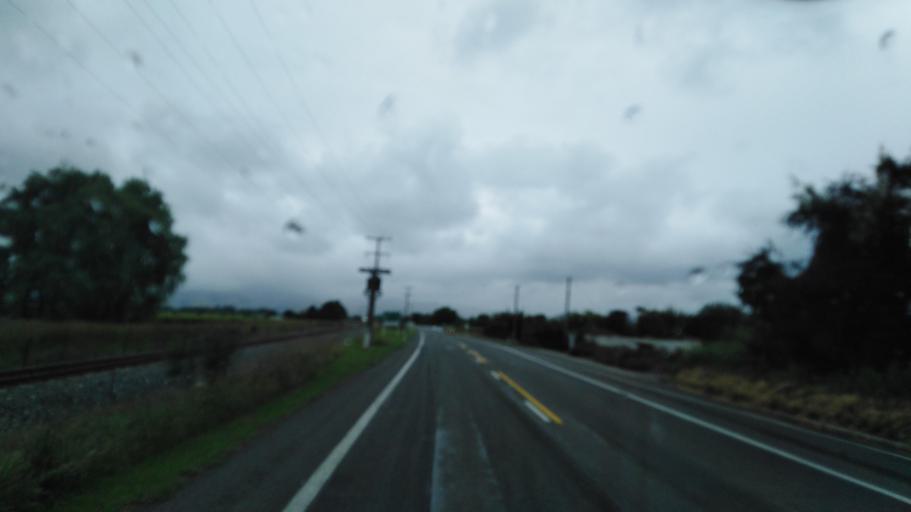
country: NZ
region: Marlborough
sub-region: Marlborough District
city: Blenheim
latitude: -41.4879
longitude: 173.9651
